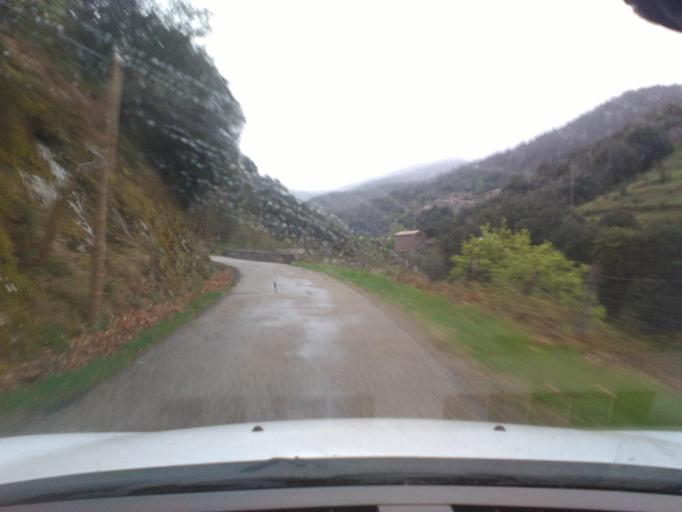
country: FR
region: Languedoc-Roussillon
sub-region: Departement du Gard
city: Valleraugue
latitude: 44.1078
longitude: 3.6956
